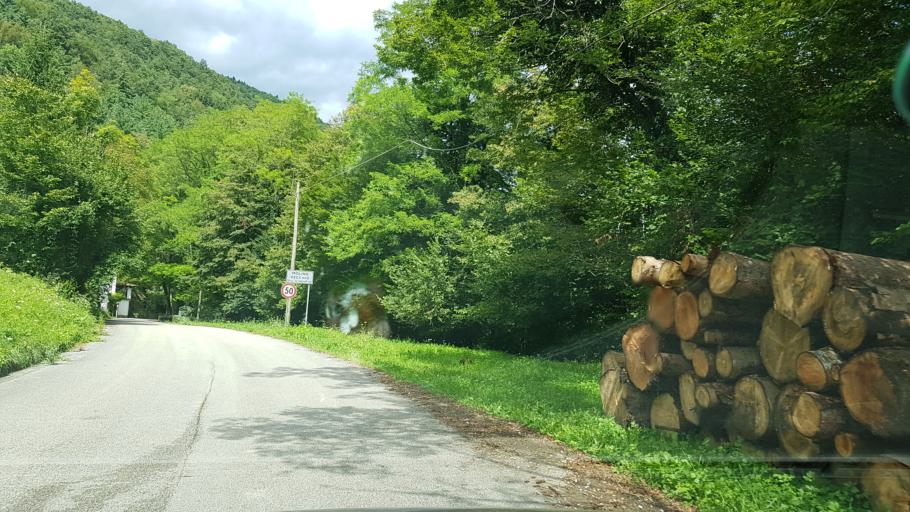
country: IT
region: Friuli Venezia Giulia
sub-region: Provincia di Udine
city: Stregna
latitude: 46.0968
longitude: 13.5786
